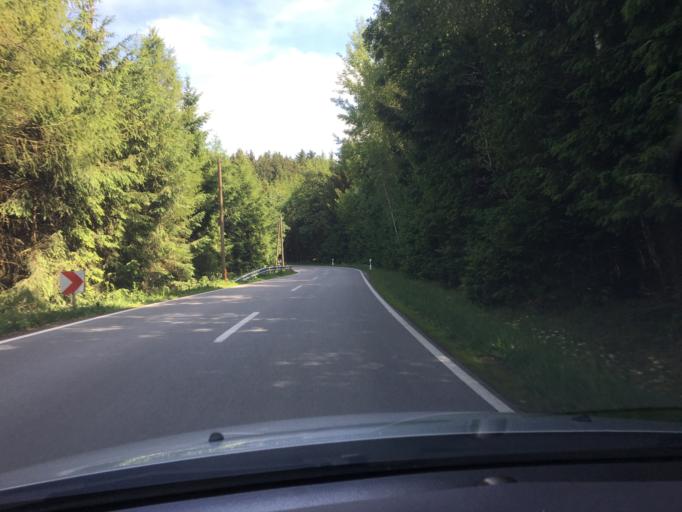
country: DE
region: Bavaria
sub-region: Upper Bavaria
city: Niedertaufkirchen
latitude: 48.3426
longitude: 12.5806
